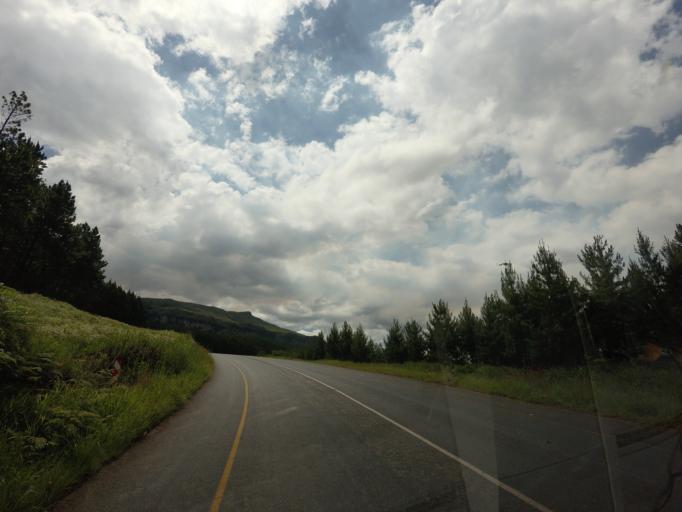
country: ZA
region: Mpumalanga
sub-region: Ehlanzeni District
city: Graksop
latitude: -24.9620
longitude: 30.8133
